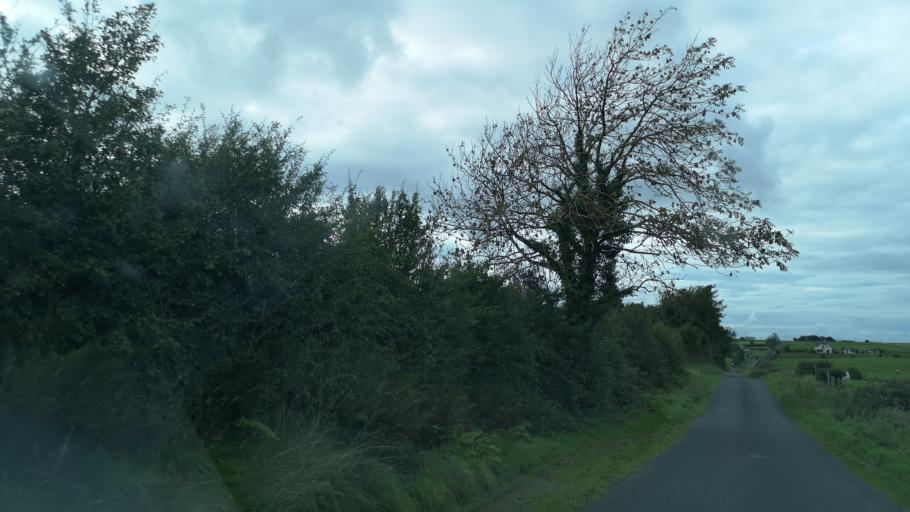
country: IE
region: Connaught
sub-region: County Galway
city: Ballinasloe
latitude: 53.3746
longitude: -8.1679
